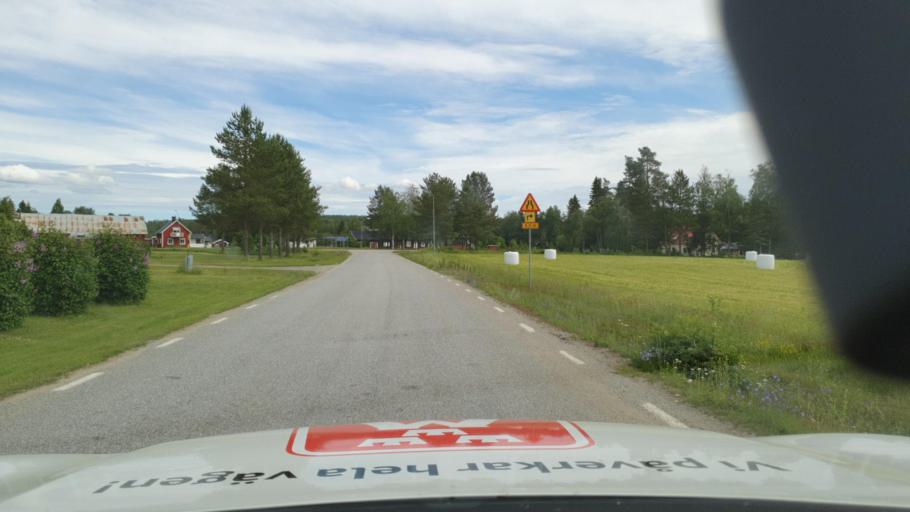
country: SE
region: Vaesterbotten
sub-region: Skelleftea Kommun
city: Burtraesk
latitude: 64.4981
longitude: 20.8556
